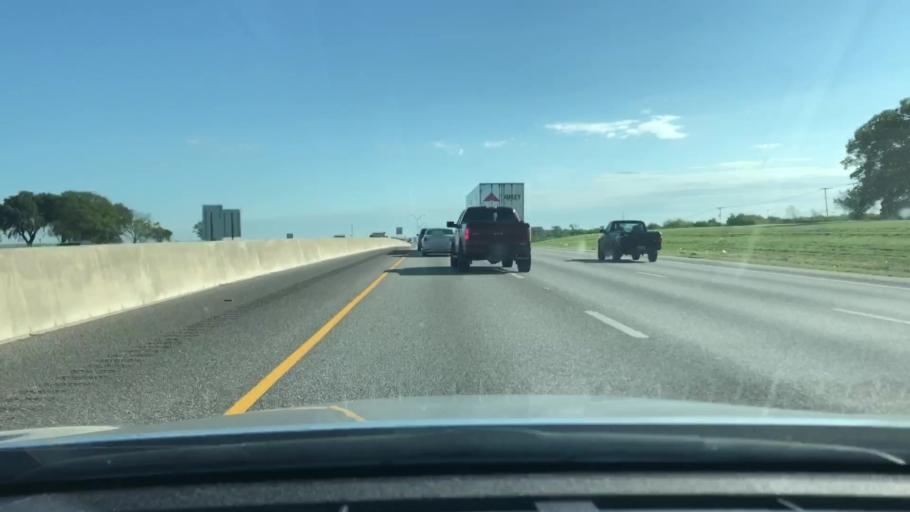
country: US
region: Texas
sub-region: Guadalupe County
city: Northcliff
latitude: 29.6328
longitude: -98.2249
